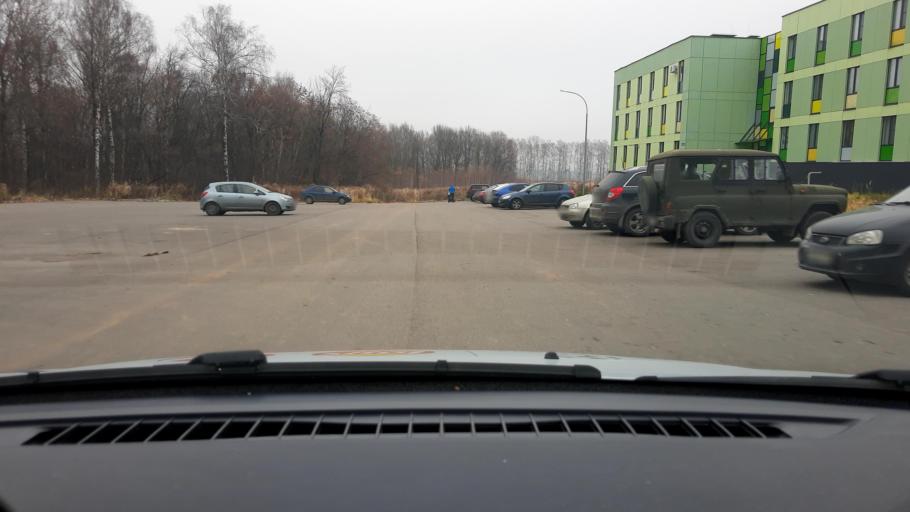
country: RU
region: Nizjnij Novgorod
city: Afonino
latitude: 56.2168
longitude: 44.0155
